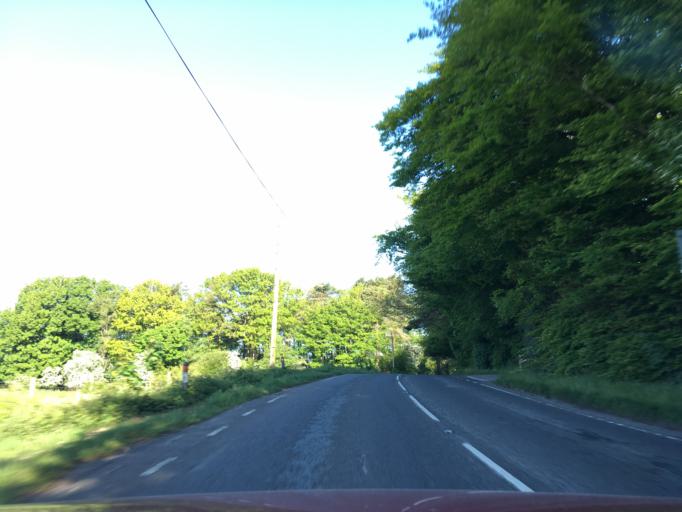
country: GB
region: England
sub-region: North Somerset
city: Easton-in-Gordano
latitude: 51.4455
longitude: -2.7059
